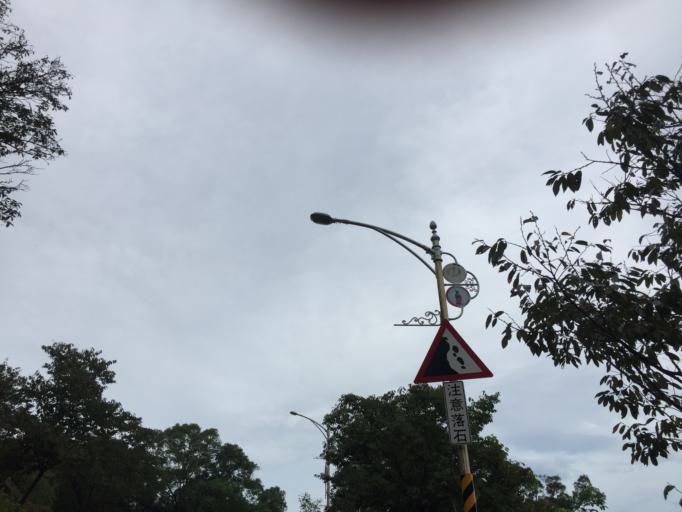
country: TW
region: Taipei
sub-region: Taipei
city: Banqiao
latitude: 24.9729
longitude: 121.5005
